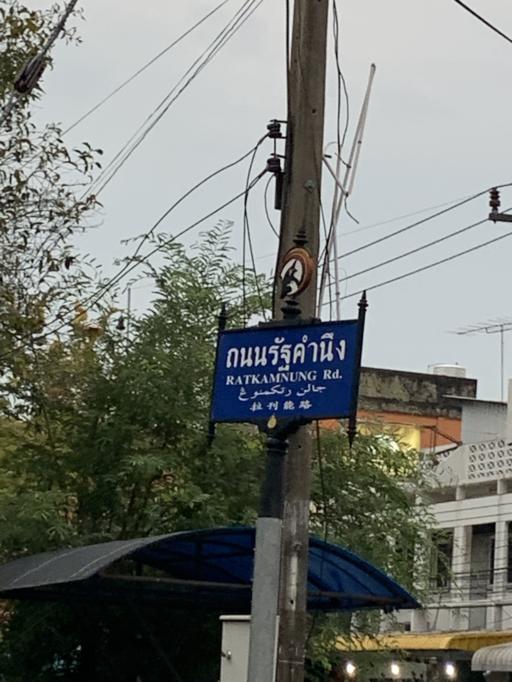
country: TH
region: Yala
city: Yala
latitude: 6.5497
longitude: 101.2858
